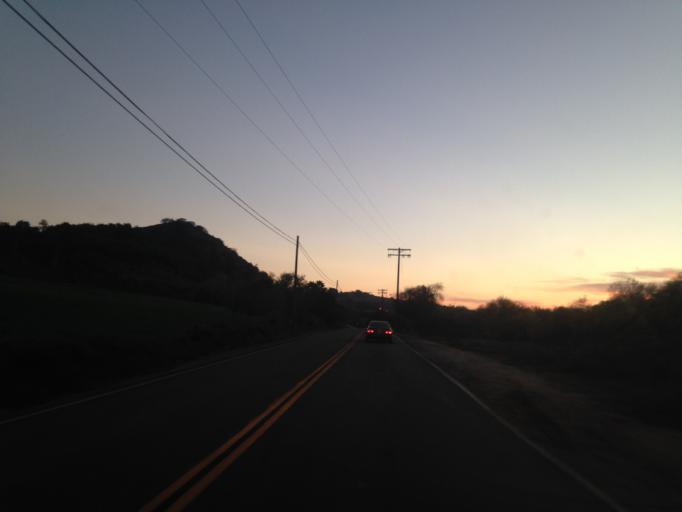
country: US
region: California
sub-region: San Diego County
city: Bonsall
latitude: 33.2654
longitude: -117.2334
